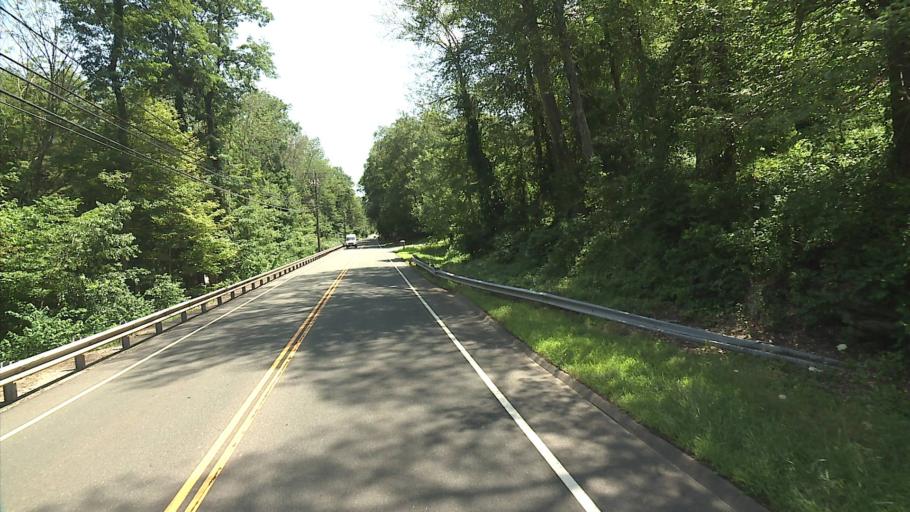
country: US
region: Connecticut
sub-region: Middlesex County
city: East Haddam
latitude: 41.4336
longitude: -72.4563
